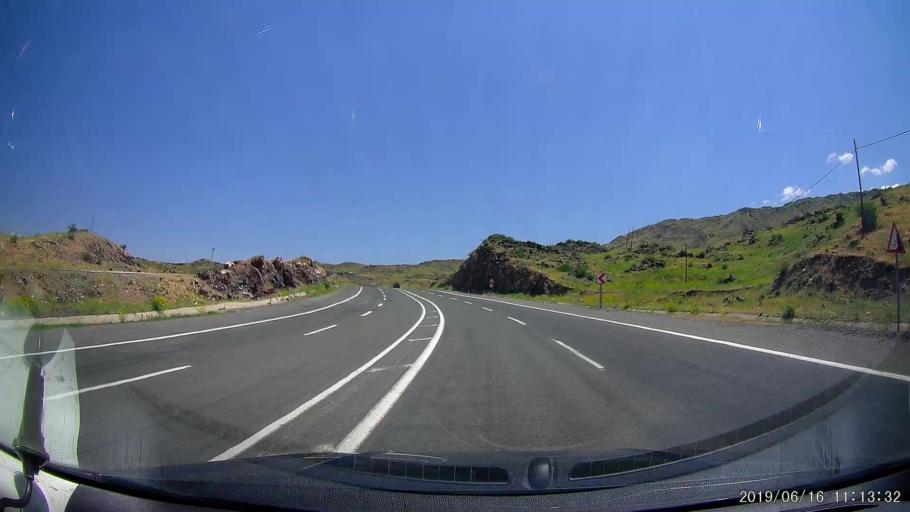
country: TR
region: Igdir
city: Igdir
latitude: 39.7844
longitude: 44.1398
